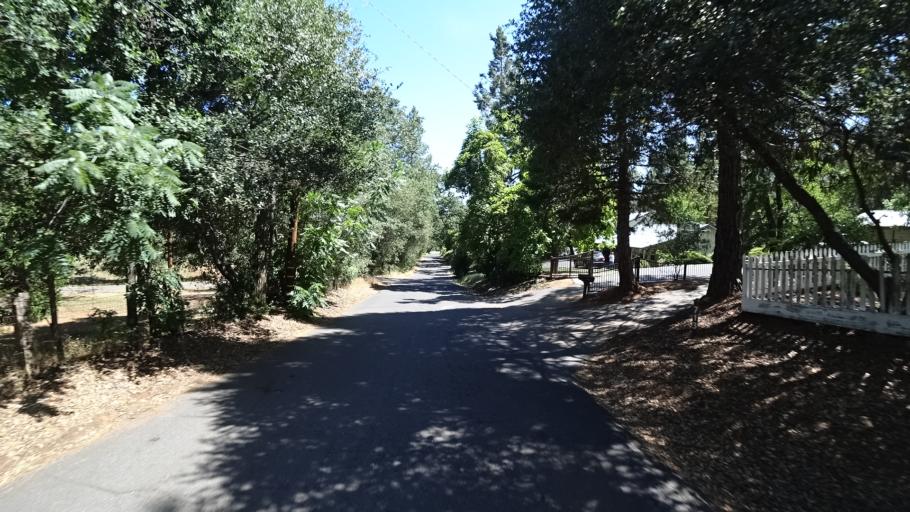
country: US
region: California
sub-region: Calaveras County
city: Murphys
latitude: 38.1412
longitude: -120.4661
